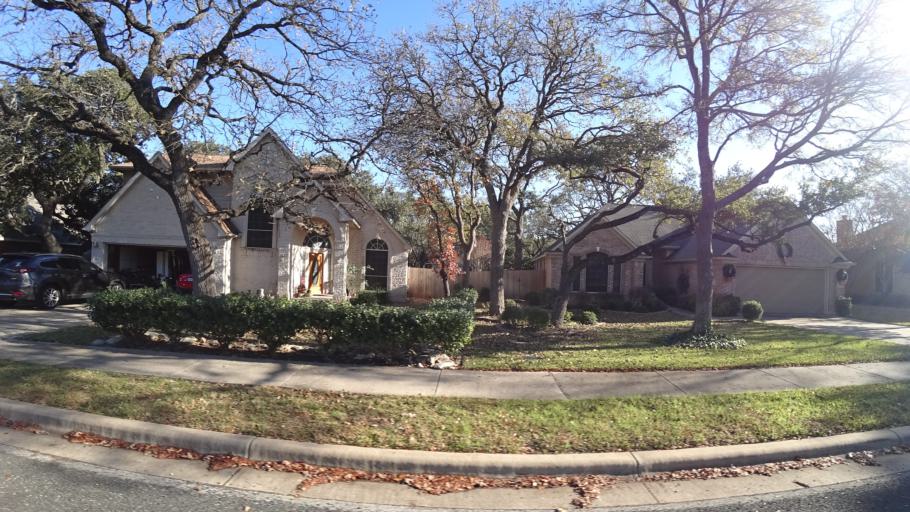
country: US
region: Texas
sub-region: Williamson County
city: Brushy Creek
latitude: 30.4938
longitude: -97.7459
